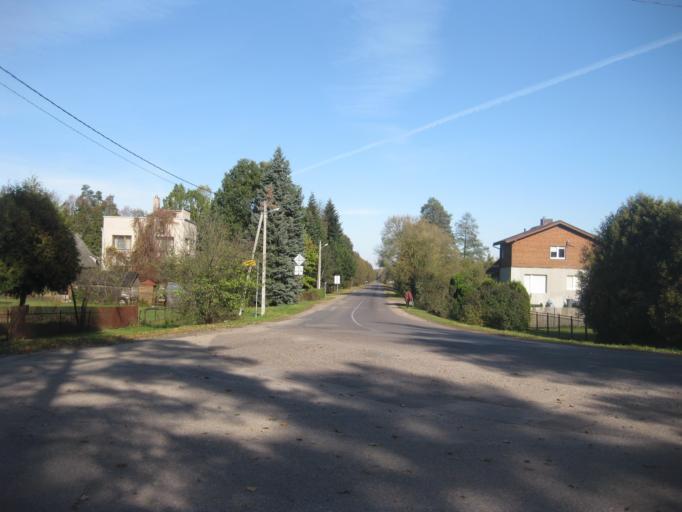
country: LT
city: Ezerelis
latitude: 54.8839
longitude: 23.5990
